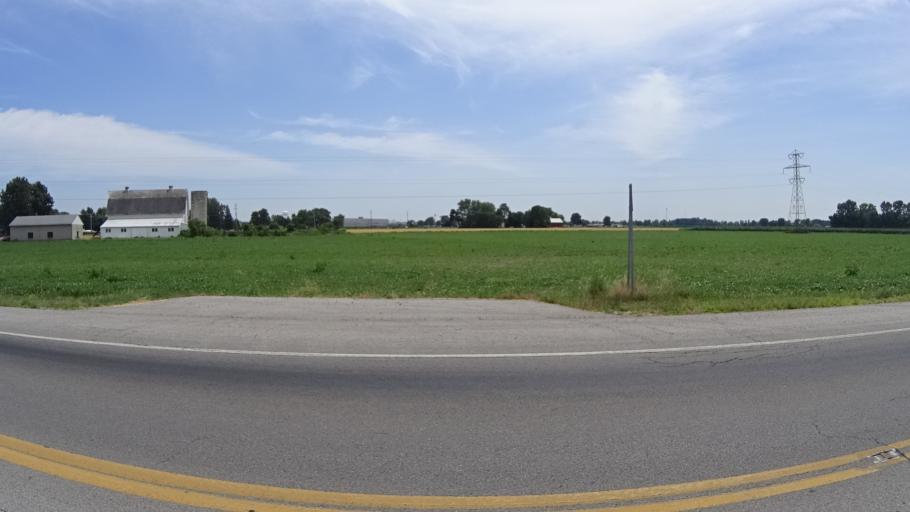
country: US
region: Ohio
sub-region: Erie County
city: Sandusky
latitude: 41.4340
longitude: -82.7453
